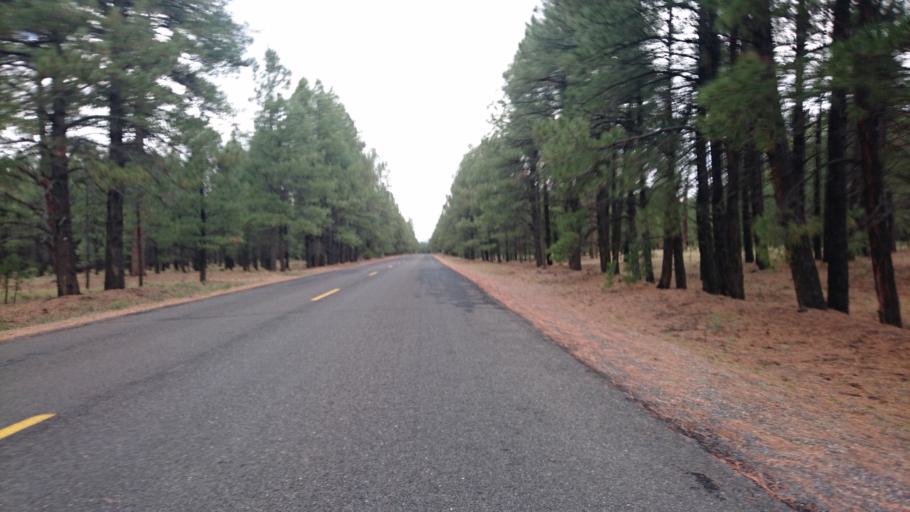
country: US
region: Arizona
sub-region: Coconino County
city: Parks
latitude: 35.2588
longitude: -111.8686
